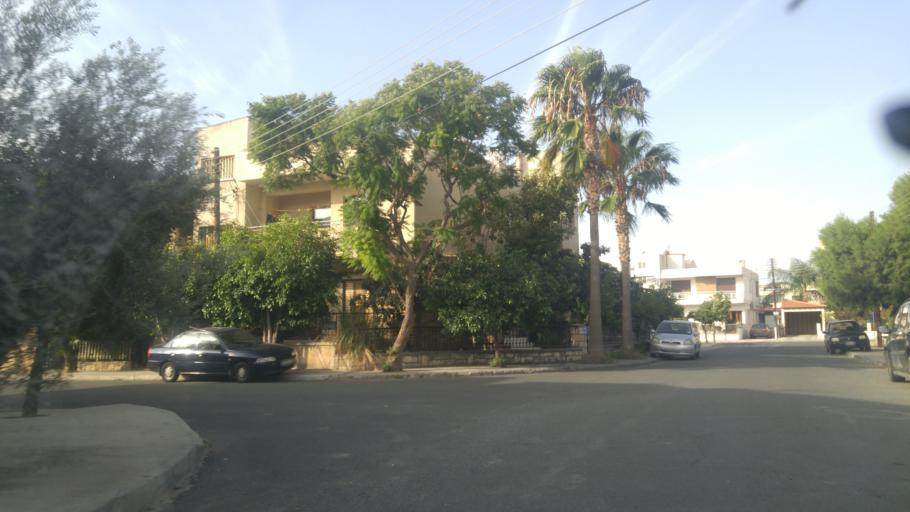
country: CY
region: Limassol
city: Limassol
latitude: 34.6638
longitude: 33.0050
